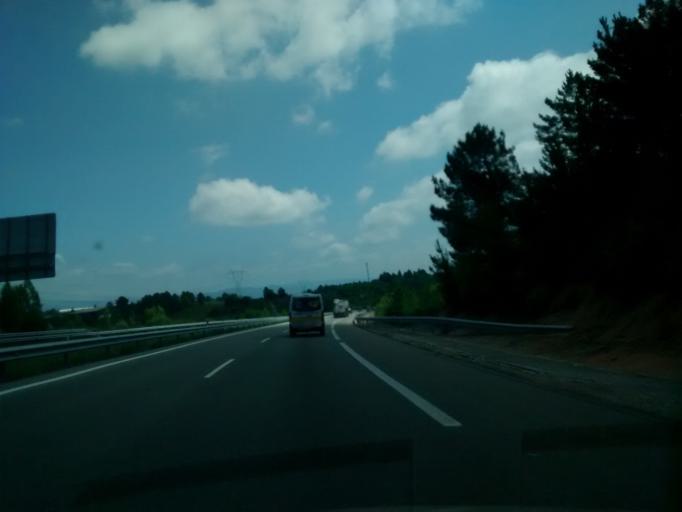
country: ES
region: Castille and Leon
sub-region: Provincia de Leon
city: Molinaseca
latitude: 42.5687
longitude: -6.5453
